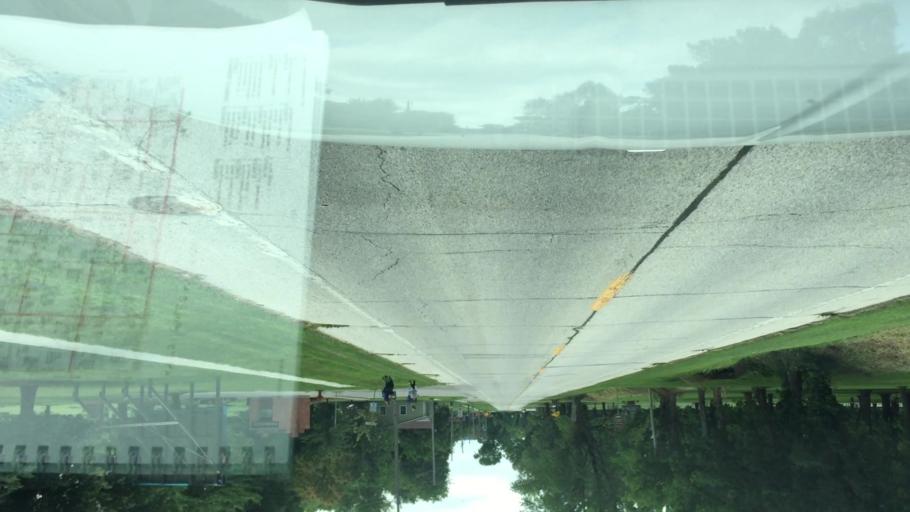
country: US
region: Illinois
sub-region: Hancock County
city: Nauvoo
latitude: 40.5447
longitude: -91.3866
